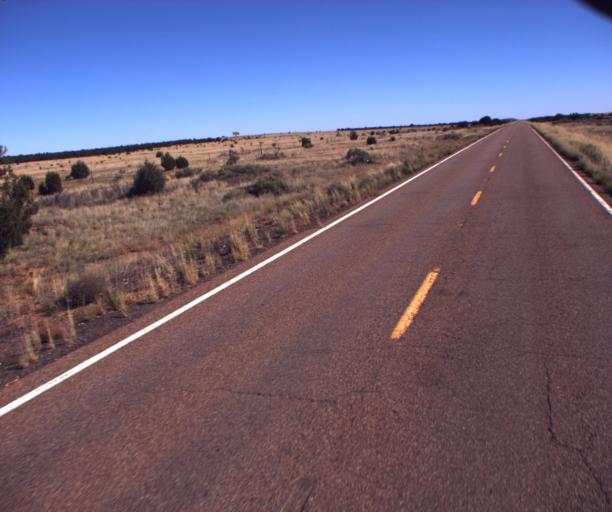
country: US
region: Arizona
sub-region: Navajo County
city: Heber-Overgaard
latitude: 34.4753
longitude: -110.3512
